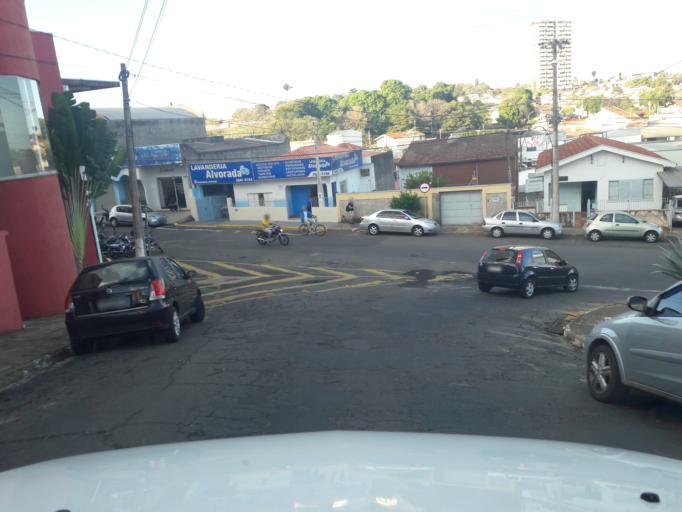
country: BR
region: Sao Paulo
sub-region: Moji-Guacu
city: Mogi-Gaucu
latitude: -22.3694
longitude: -46.9433
